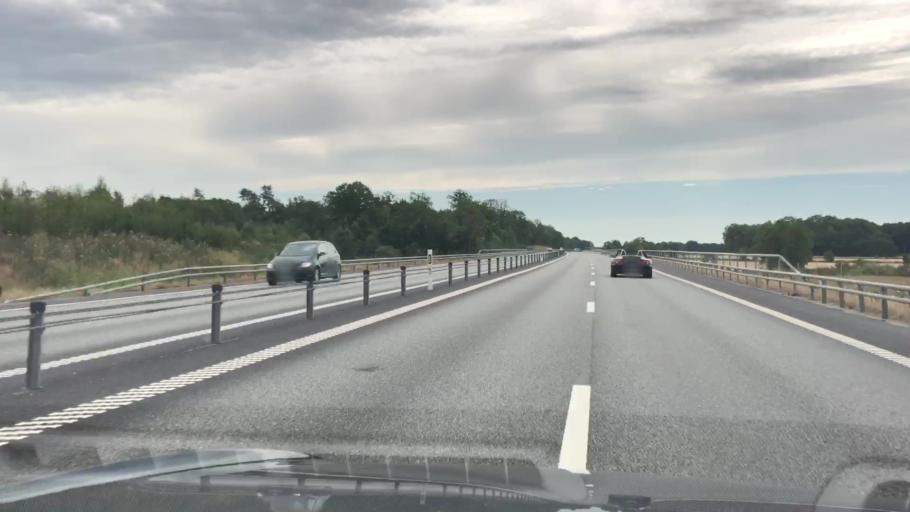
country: SE
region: Blekinge
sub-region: Karlshamns Kommun
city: Morrum
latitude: 56.1526
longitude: 14.6646
